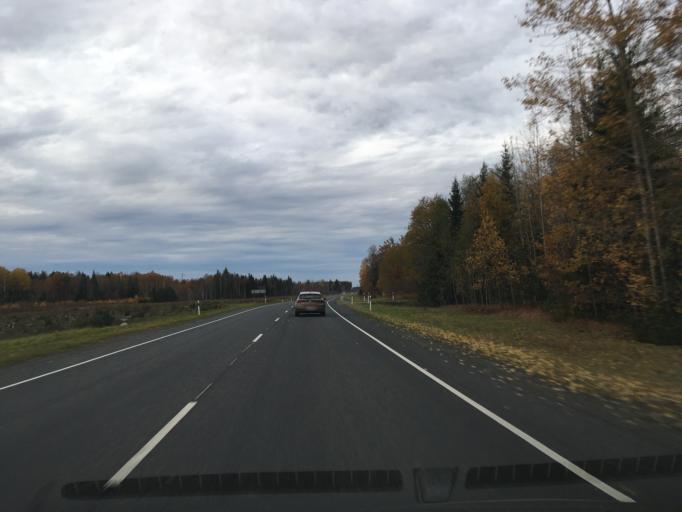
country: EE
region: Harju
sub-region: Nissi vald
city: Turba
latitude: 58.9401
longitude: 24.0895
